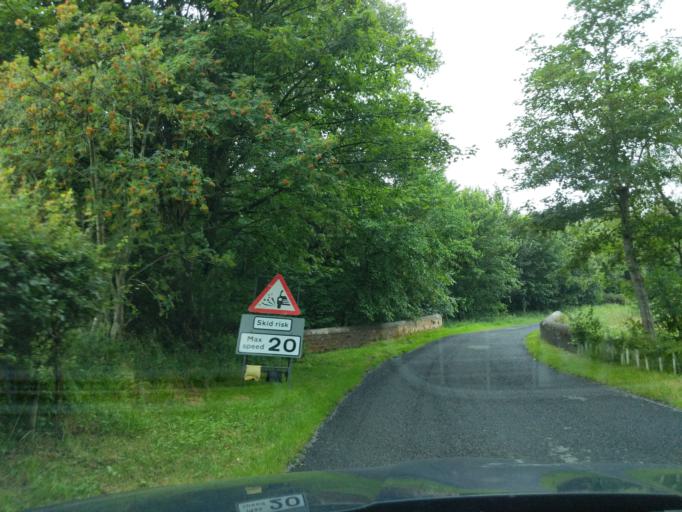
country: GB
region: England
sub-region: Northumberland
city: Ford
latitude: 55.7027
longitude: -2.1455
